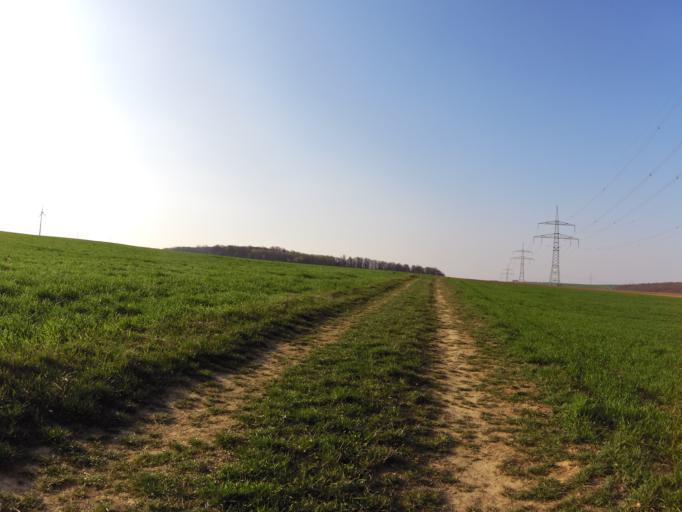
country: DE
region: Bavaria
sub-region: Regierungsbezirk Unterfranken
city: Theilheim
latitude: 49.7687
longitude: 10.0507
